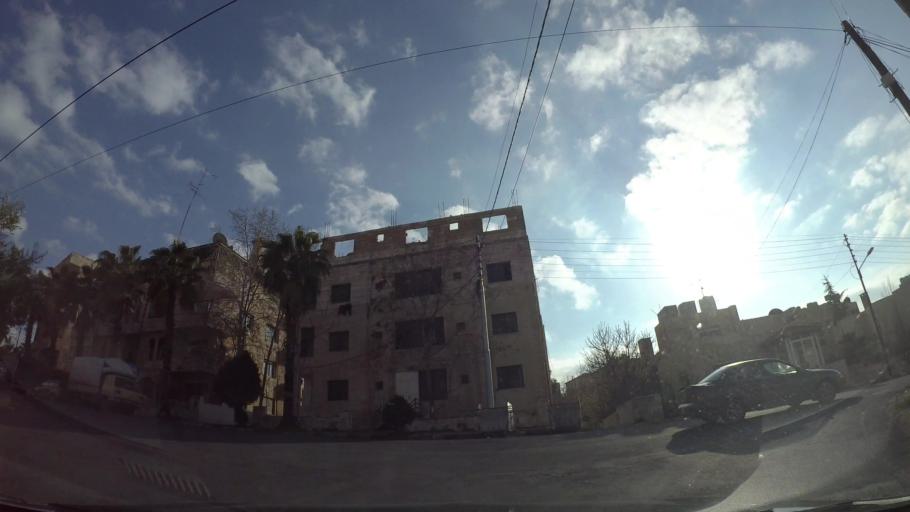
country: JO
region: Amman
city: Al Jubayhah
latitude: 31.9855
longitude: 35.8752
